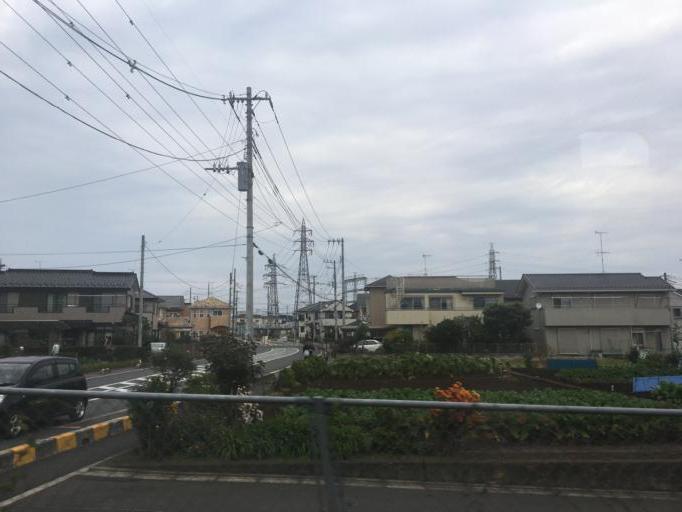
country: JP
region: Saitama
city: Hanno
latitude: 35.8464
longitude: 139.3293
